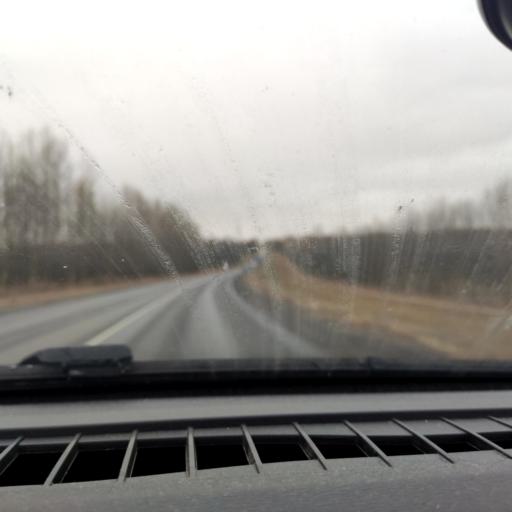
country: RU
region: Belgorod
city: Alekseyevka
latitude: 50.6486
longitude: 38.6735
